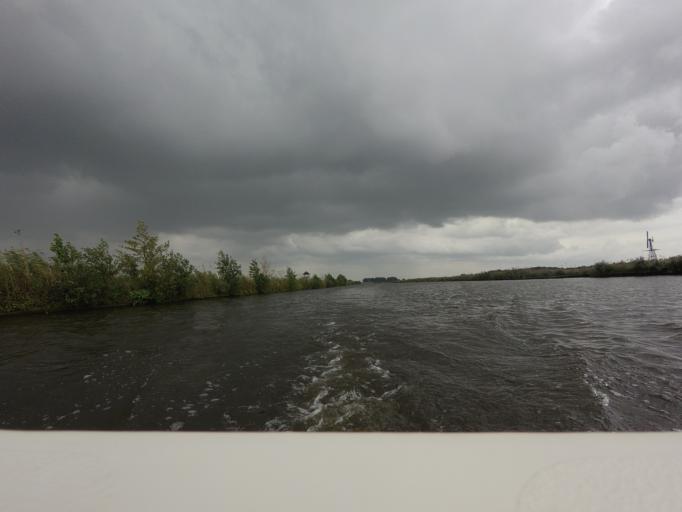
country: NL
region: Friesland
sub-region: Gemeente Smallingerland
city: Oudega
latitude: 53.1169
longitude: 5.9462
